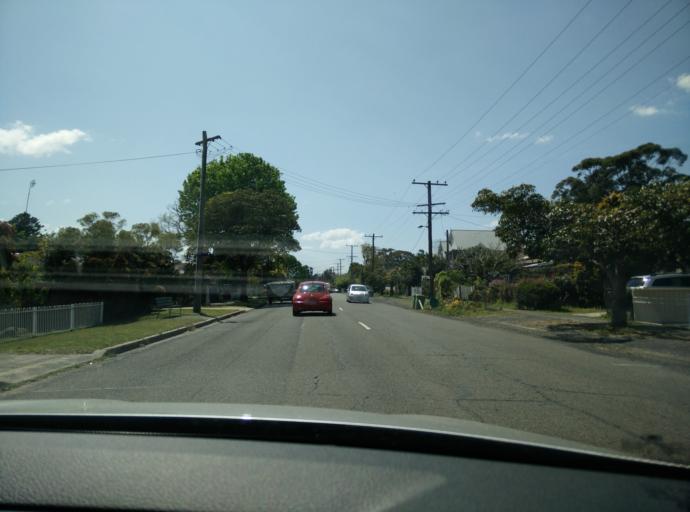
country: AU
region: New South Wales
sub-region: Gosford Shire
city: Blackwall
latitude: -33.4942
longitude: 151.3105
